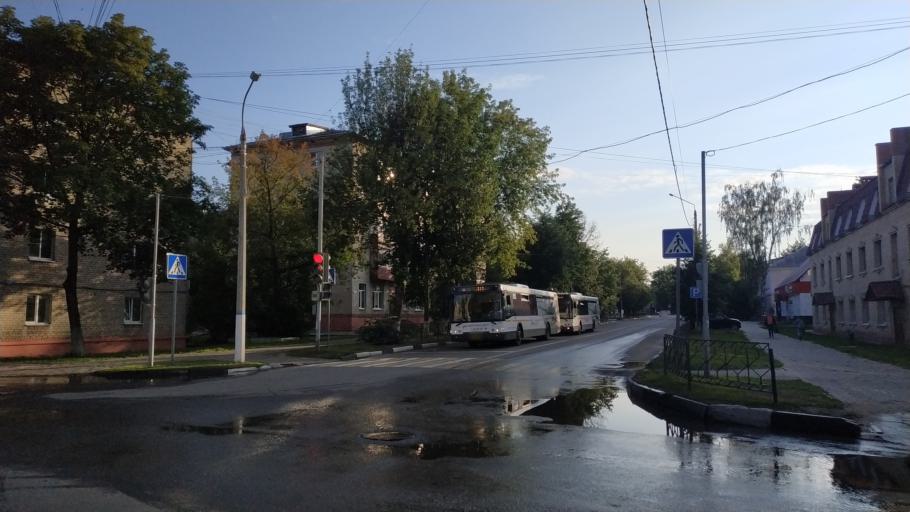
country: RU
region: Moskovskaya
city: Shatura
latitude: 55.5756
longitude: 39.5451
